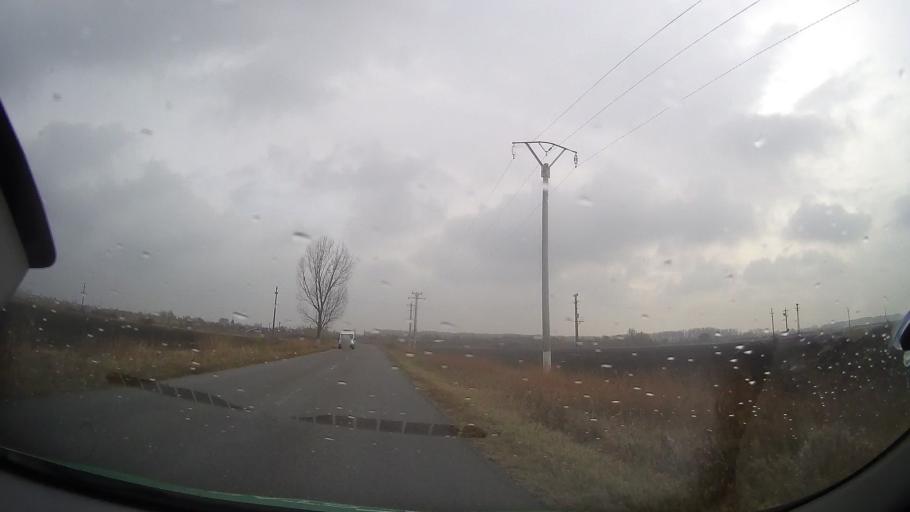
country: RO
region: Prahova
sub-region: Comuna Draganesti
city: Draganesti
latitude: 44.8312
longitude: 26.2749
